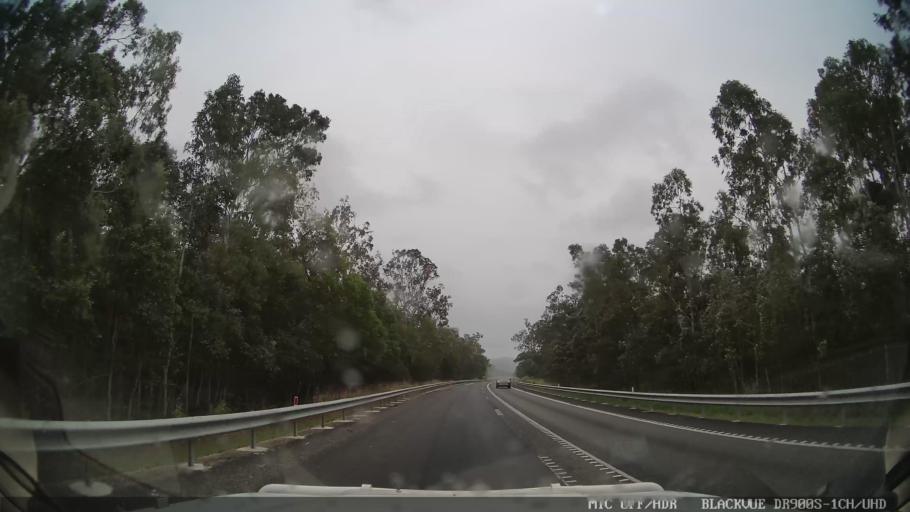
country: AU
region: Queensland
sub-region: Hinchinbrook
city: Ingham
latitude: -18.2115
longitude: 145.9653
